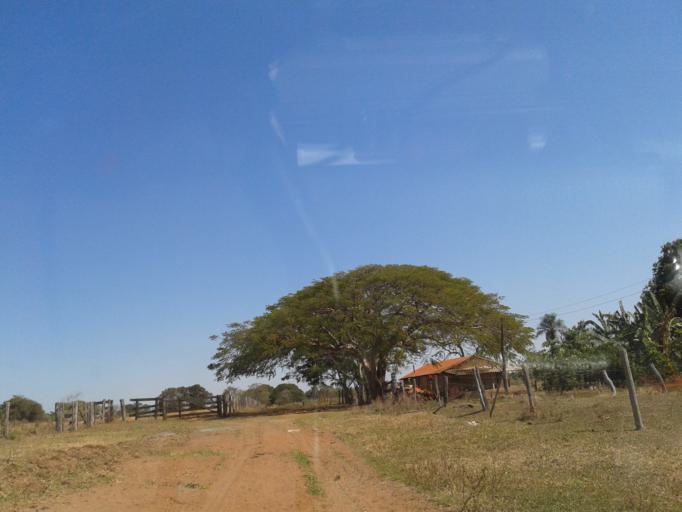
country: BR
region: Minas Gerais
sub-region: Santa Vitoria
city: Santa Vitoria
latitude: -19.0878
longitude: -50.0761
